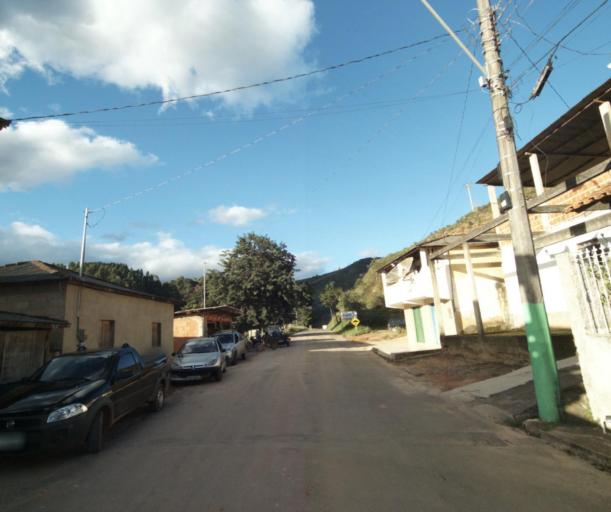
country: BR
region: Espirito Santo
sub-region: Guacui
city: Guacui
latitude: -20.6172
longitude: -41.6811
